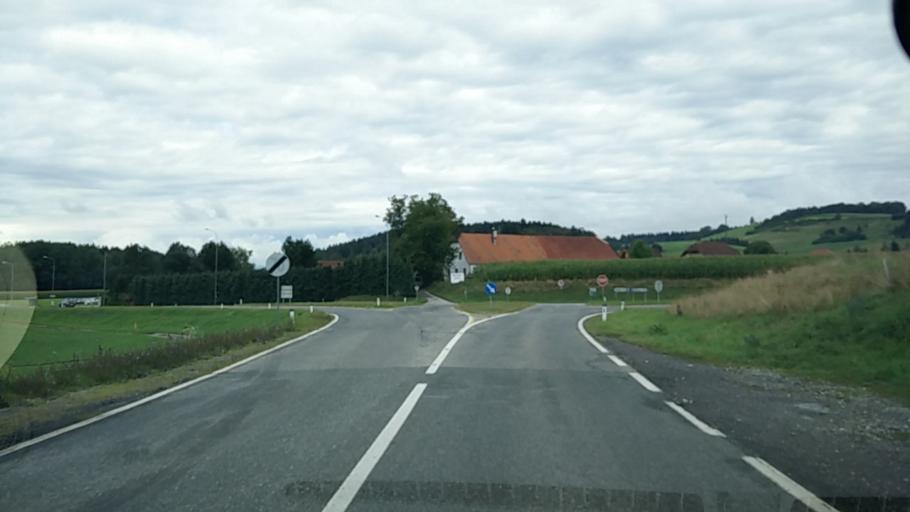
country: AT
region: Carinthia
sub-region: Politischer Bezirk Klagenfurt Land
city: Poggersdorf
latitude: 46.6488
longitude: 14.5060
